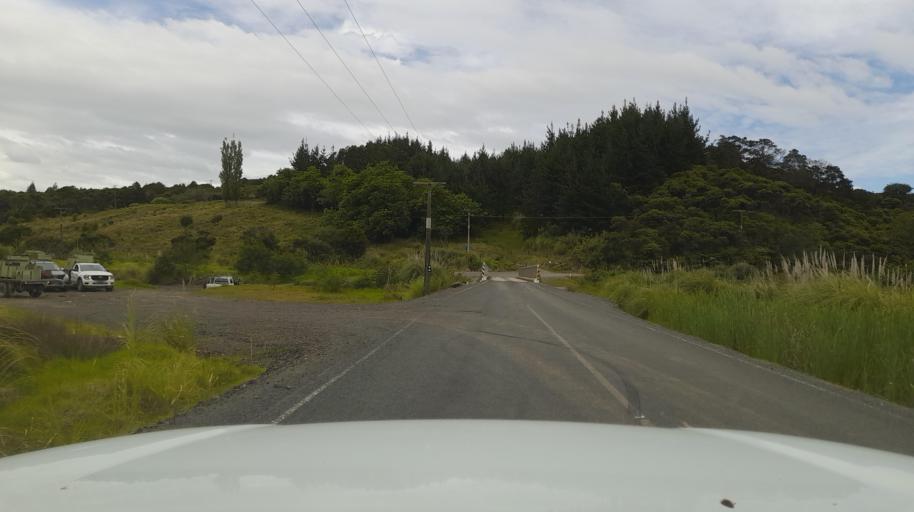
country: NZ
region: Northland
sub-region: Far North District
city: Kaitaia
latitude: -35.4074
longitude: 173.3825
